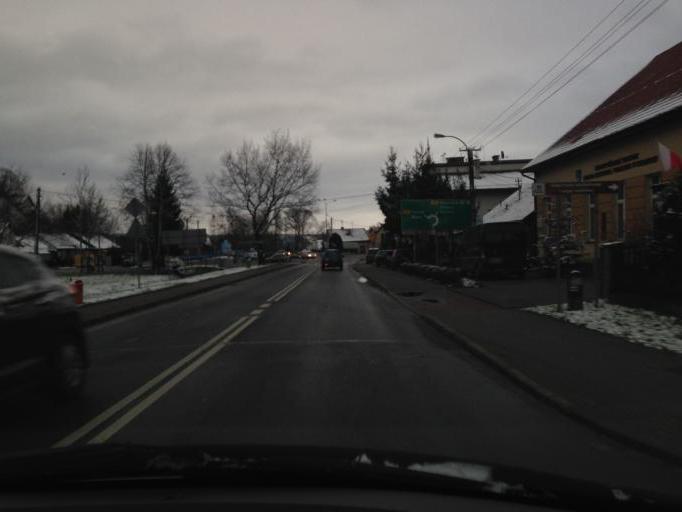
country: PL
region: Lesser Poland Voivodeship
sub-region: Powiat tarnowski
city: Gromnik
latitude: 49.8385
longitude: 20.9593
